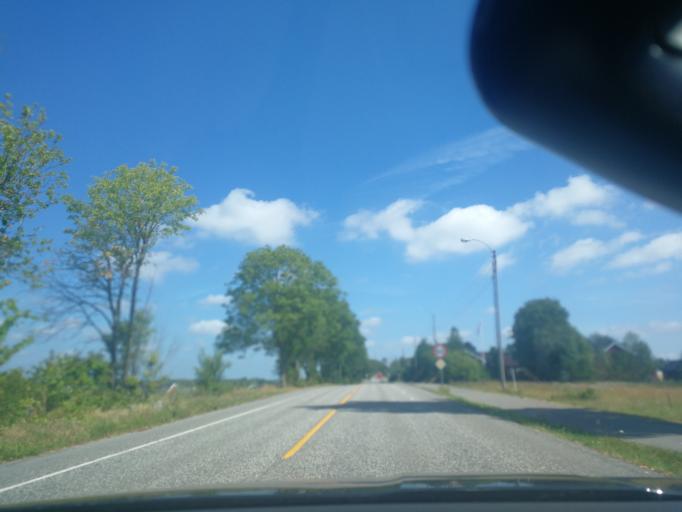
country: NO
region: Vestfold
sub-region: Sandefjord
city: Sandefjord
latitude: 59.1882
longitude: 10.2214
